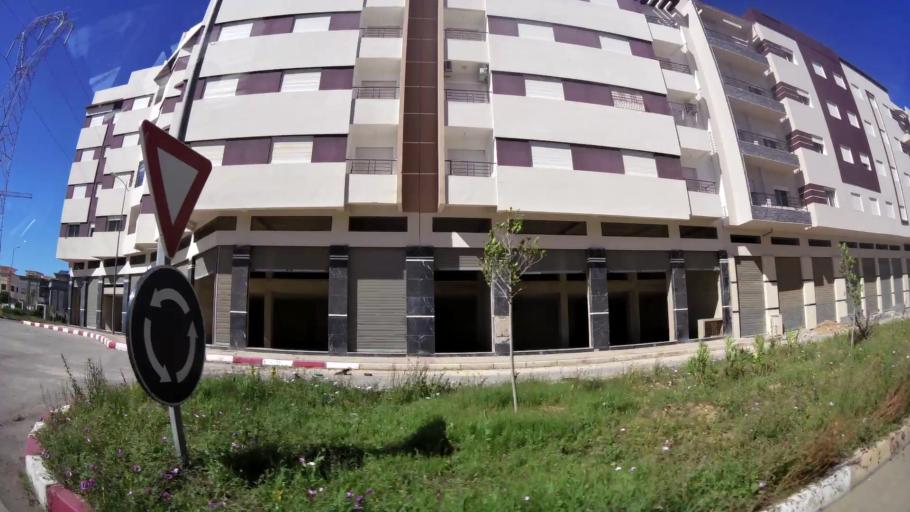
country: MA
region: Oriental
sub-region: Oujda-Angad
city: Oujda
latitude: 34.7230
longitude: -1.9095
